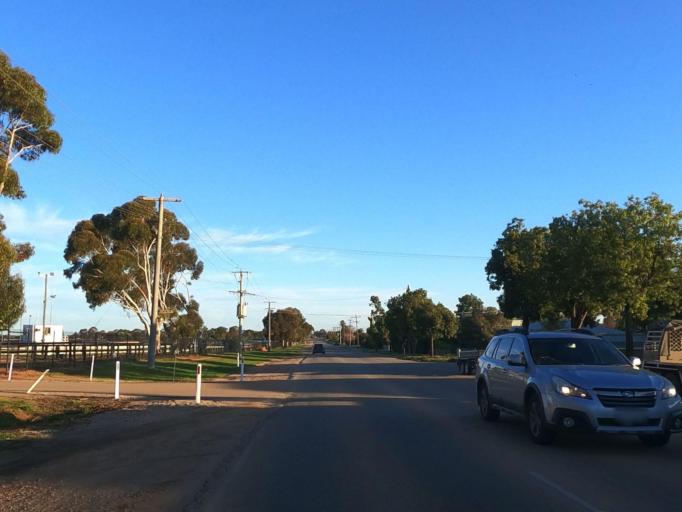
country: AU
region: Victoria
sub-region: Swan Hill
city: Swan Hill
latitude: -35.3481
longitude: 143.5552
